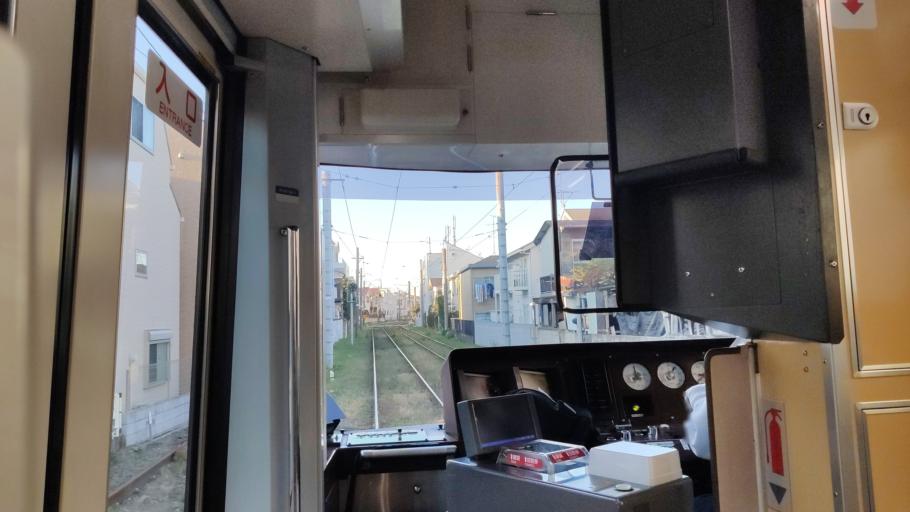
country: JP
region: Tokyo
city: Tokyo
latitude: 35.6451
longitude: 139.6453
